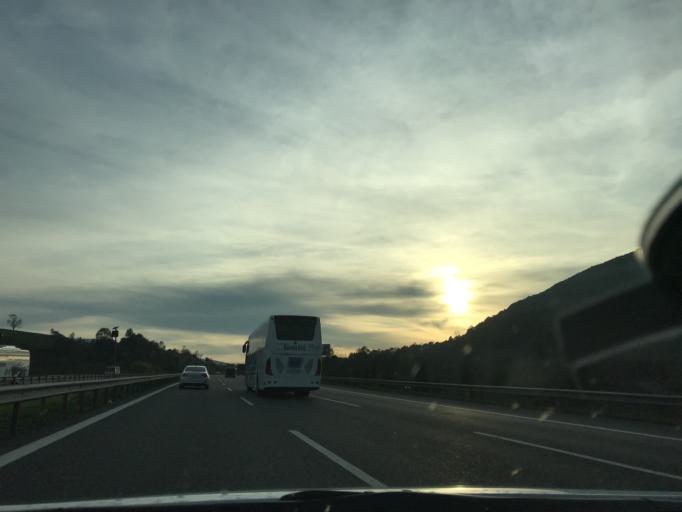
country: TR
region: Duzce
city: Gumusova
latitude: 40.8214
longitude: 30.9170
